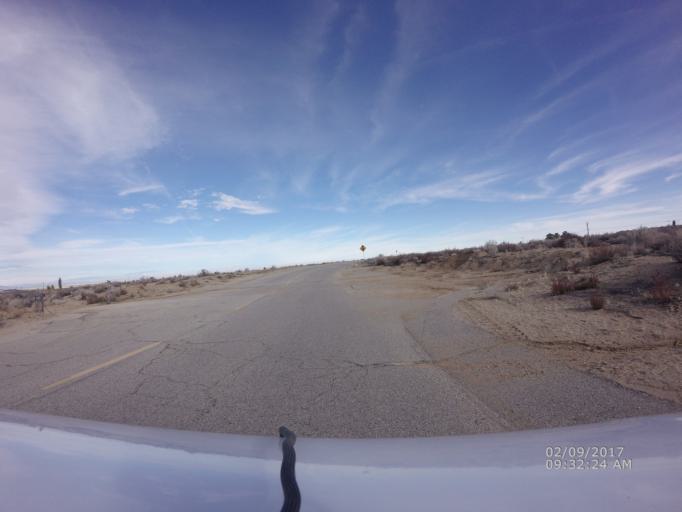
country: US
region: California
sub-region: Los Angeles County
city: Lake Los Angeles
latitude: 34.4764
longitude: -117.8370
